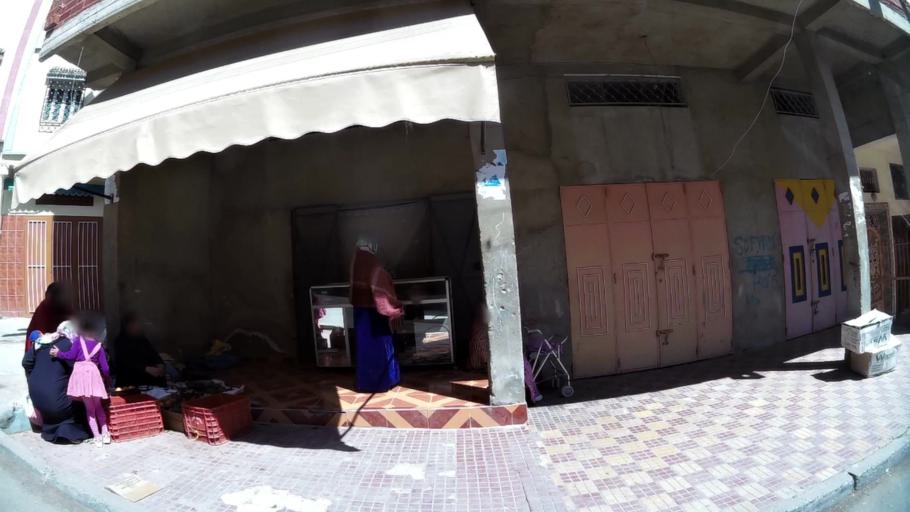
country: MA
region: Tanger-Tetouan
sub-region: Tanger-Assilah
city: Tangier
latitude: 35.7581
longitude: -5.8075
